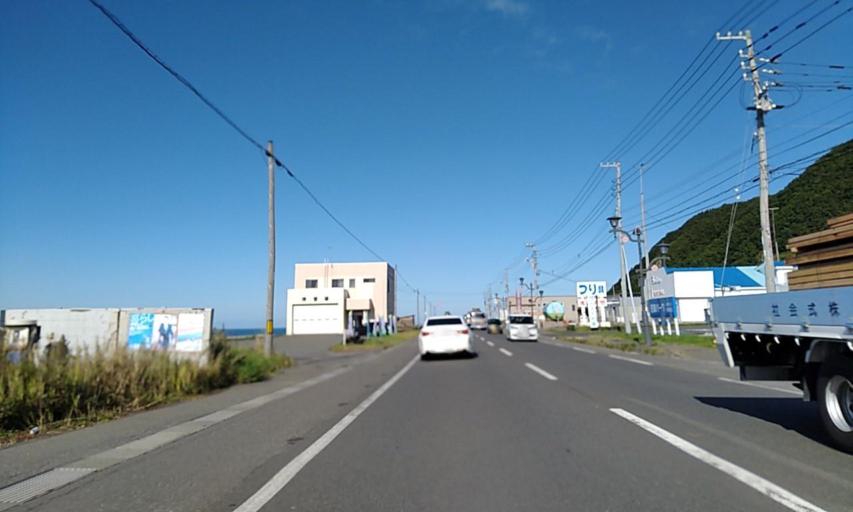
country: JP
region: Hokkaido
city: Shizunai-furukawacho
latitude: 42.3426
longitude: 142.3413
